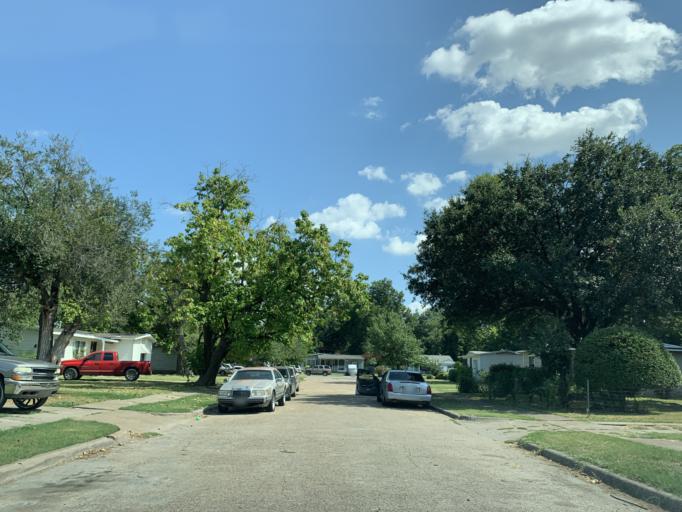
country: US
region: Texas
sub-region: Dallas County
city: Hutchins
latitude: 32.7030
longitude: -96.7661
